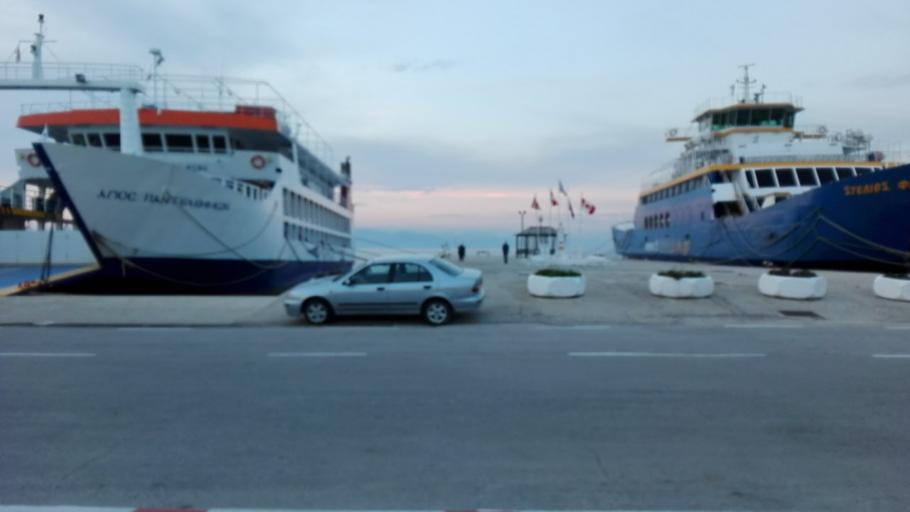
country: GR
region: East Macedonia and Thrace
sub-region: Nomos Kavalas
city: Prinos
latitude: 40.7587
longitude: 24.5773
